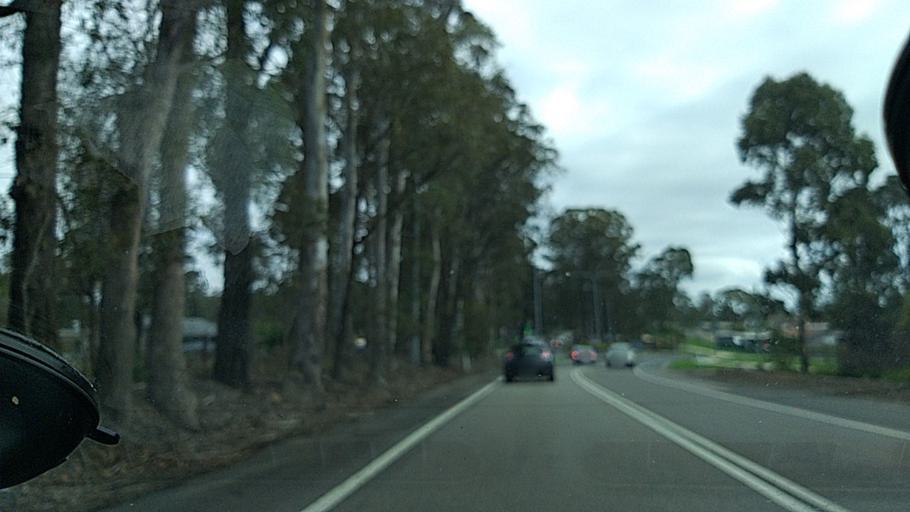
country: AU
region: New South Wales
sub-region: Wollondilly
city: Douglas Park
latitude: -34.1928
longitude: 150.7902
